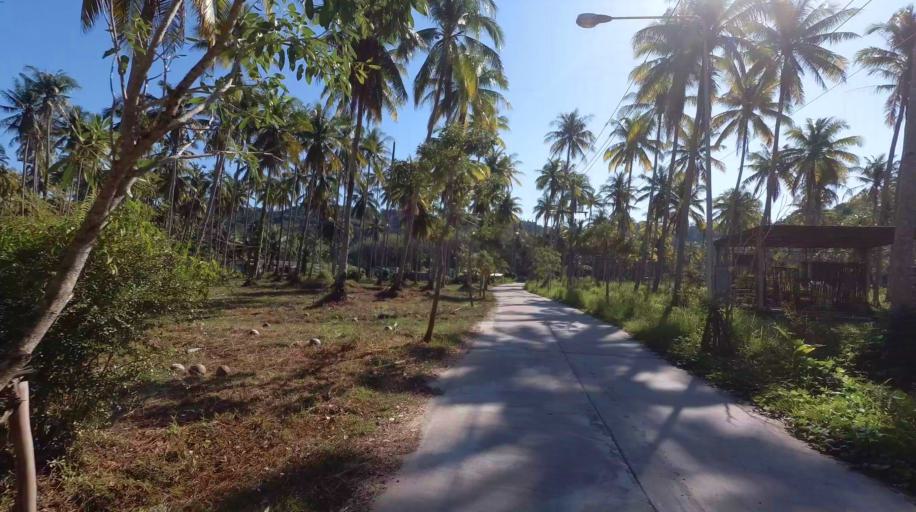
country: TH
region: Trat
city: Ko Kut
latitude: 11.6216
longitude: 102.5484
